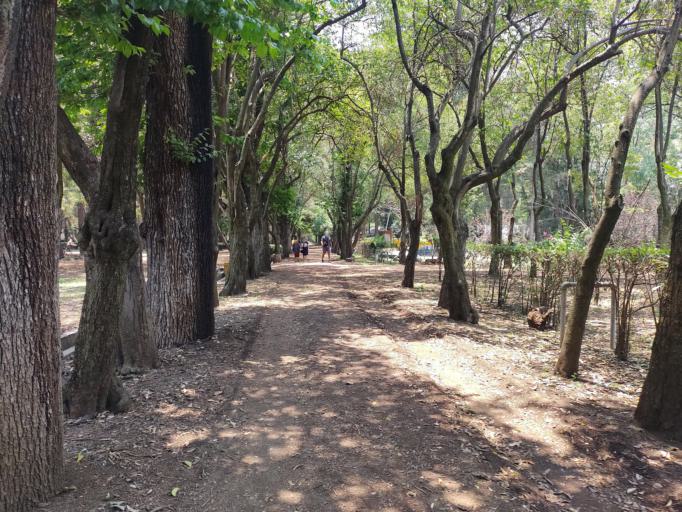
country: MX
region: Mexico City
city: Coyoacan
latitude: 19.3538
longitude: -99.1745
